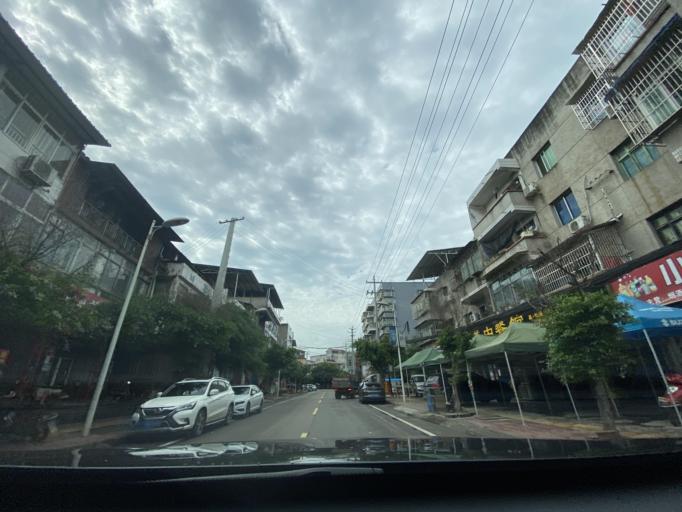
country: CN
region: Sichuan
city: Jiancheng
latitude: 30.4309
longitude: 104.6382
